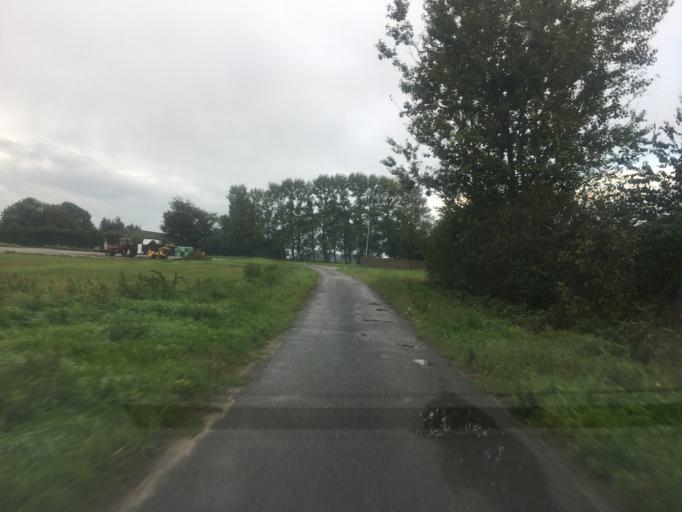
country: DK
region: South Denmark
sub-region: Tonder Kommune
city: Logumkloster
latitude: 54.9807
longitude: 8.9605
